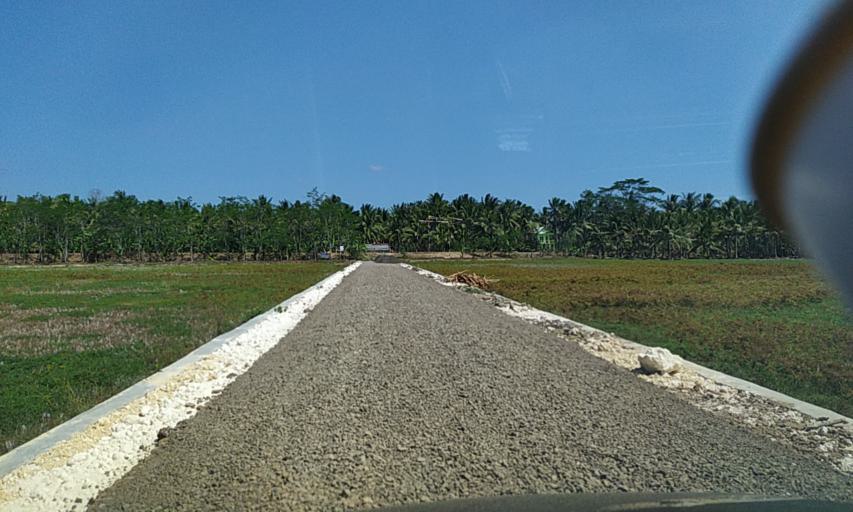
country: ID
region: Central Java
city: Cimrutu
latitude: -7.5995
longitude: 108.7954
